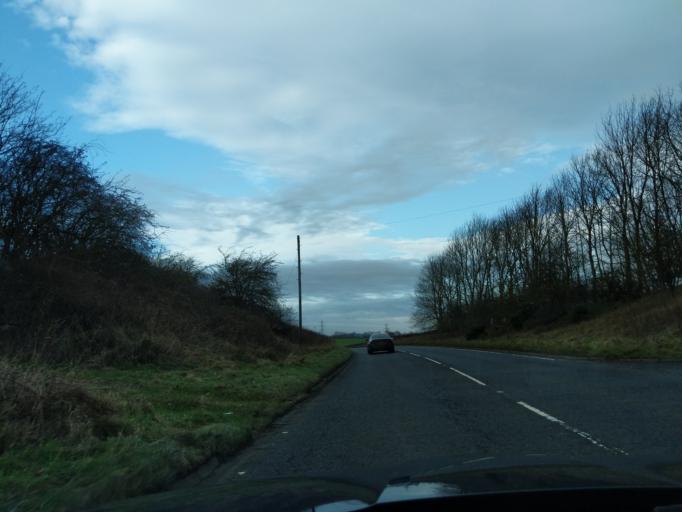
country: GB
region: England
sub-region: Northumberland
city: Meldon
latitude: 55.0963
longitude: -1.8173
